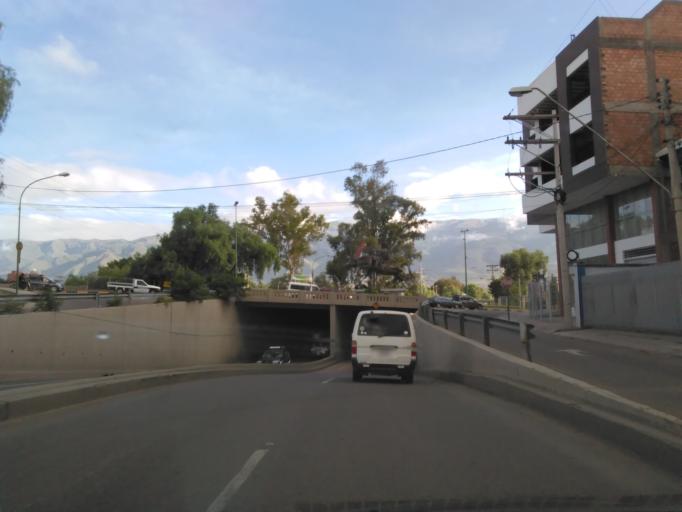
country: BO
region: Cochabamba
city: Cochabamba
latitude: -17.3946
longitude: -66.1668
